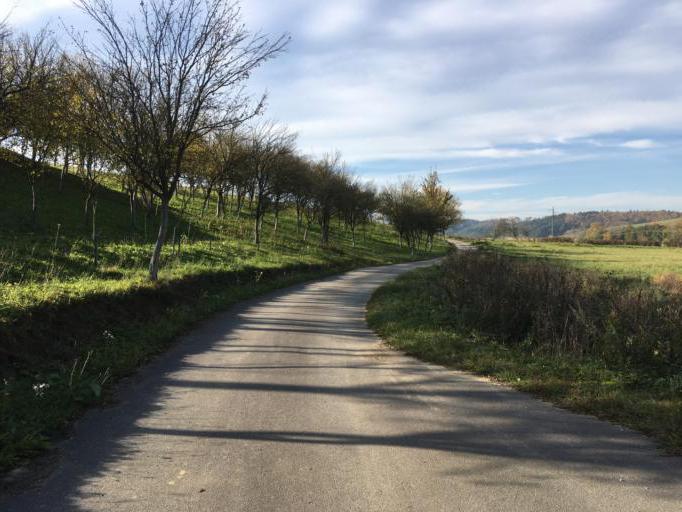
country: SK
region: Trenciansky
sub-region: Okres Povazska Bystrica
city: Povazska Bystrica
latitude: 49.0433
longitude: 18.4258
